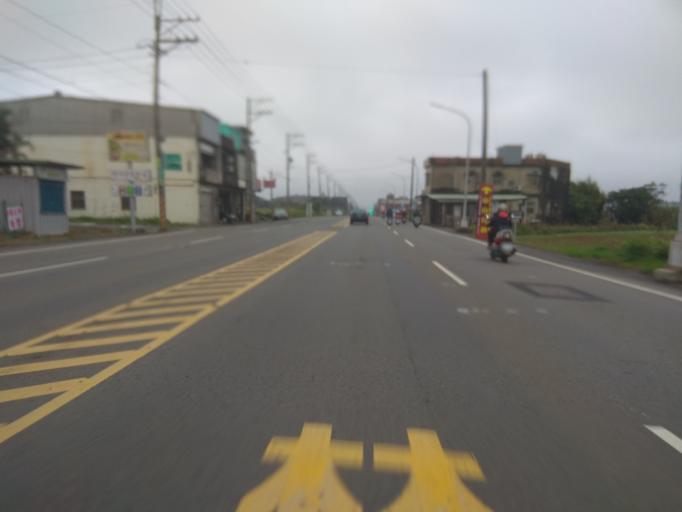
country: TW
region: Taiwan
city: Taoyuan City
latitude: 25.0235
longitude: 121.1157
